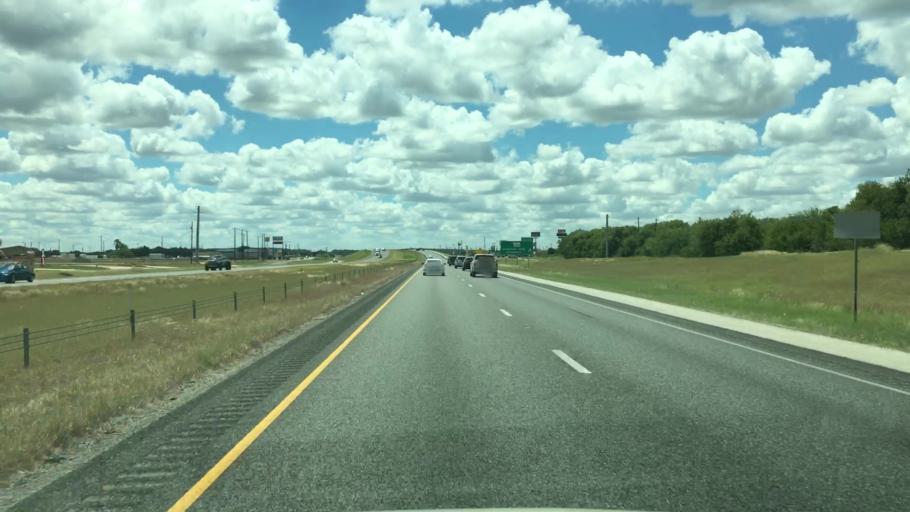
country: US
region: Texas
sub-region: Bexar County
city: Elmendorf
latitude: 29.2250
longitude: -98.4090
